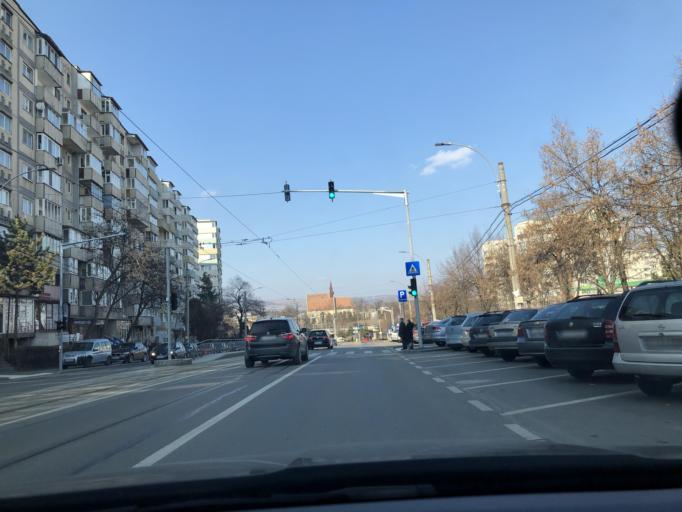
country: RO
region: Cluj
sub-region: Municipiul Cluj-Napoca
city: Cluj-Napoca
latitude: 46.7576
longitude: 23.5568
